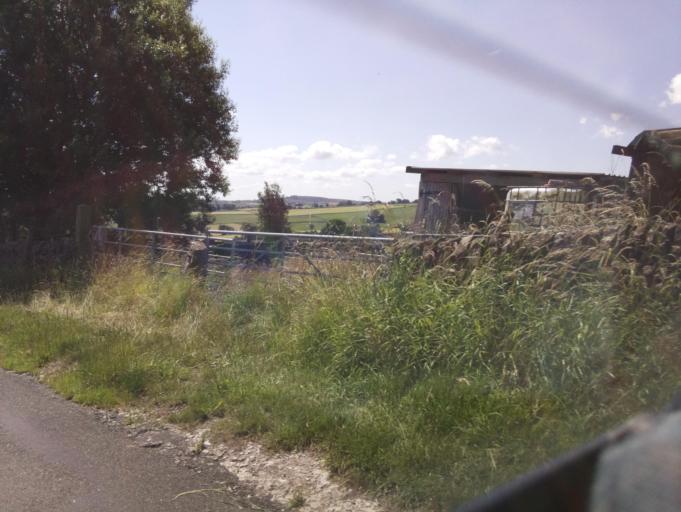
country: GB
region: England
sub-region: Derbyshire
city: Buxton
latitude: 53.1850
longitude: -1.8729
